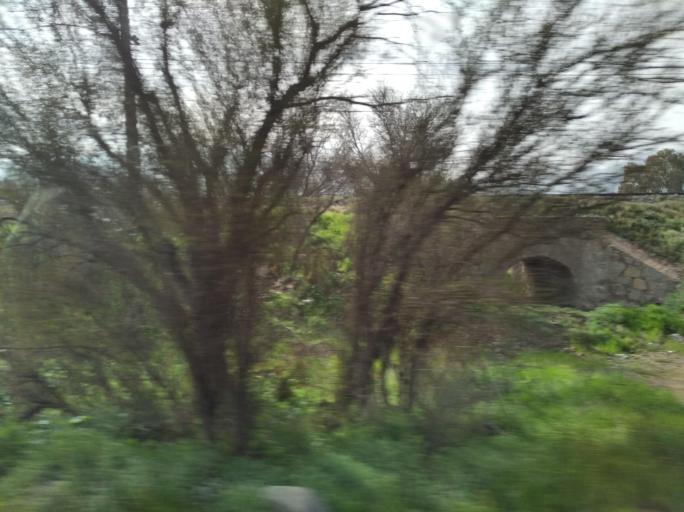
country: CL
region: Santiago Metropolitan
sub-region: Provincia de Chacabuco
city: Lampa
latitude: -33.1226
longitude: -70.9246
